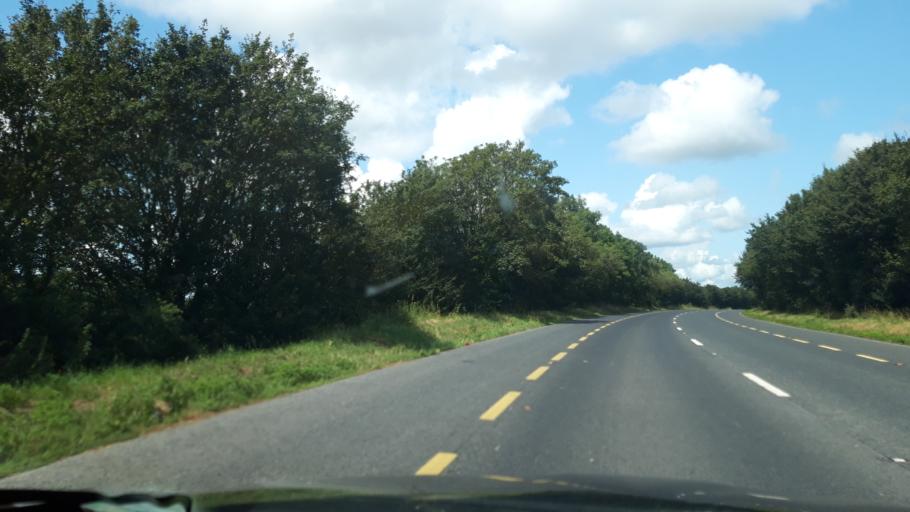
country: IE
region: Munster
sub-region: Waterford
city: Waterford
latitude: 52.2752
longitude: -7.0535
